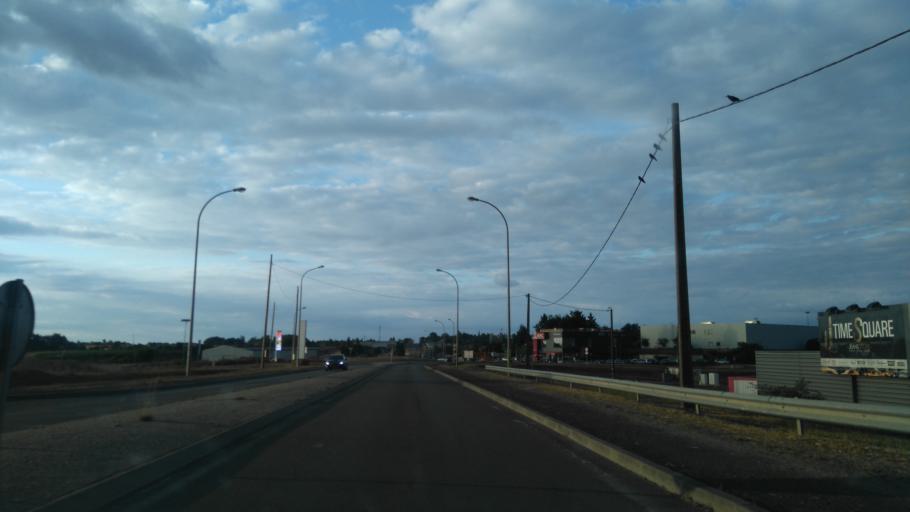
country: FR
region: Poitou-Charentes
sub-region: Departement de la Charente
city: Gond-Pontouvre
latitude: 45.6890
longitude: 0.1791
